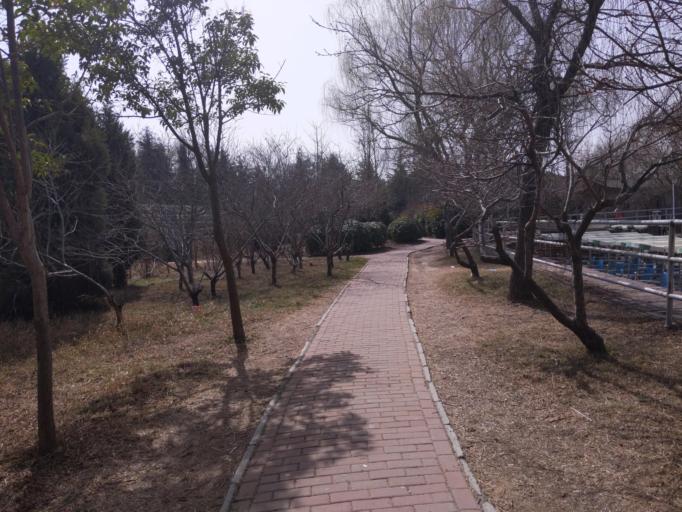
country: CN
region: Henan Sheng
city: Puyang
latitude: 35.7767
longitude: 114.9482
